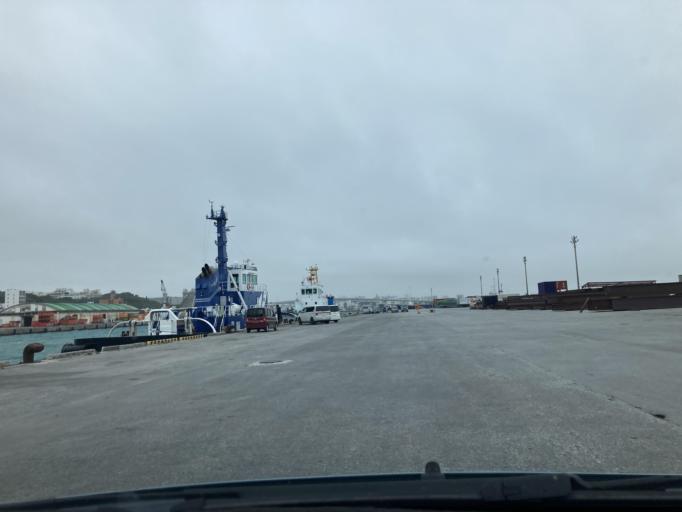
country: JP
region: Okinawa
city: Naha-shi
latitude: 26.2397
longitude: 127.6779
